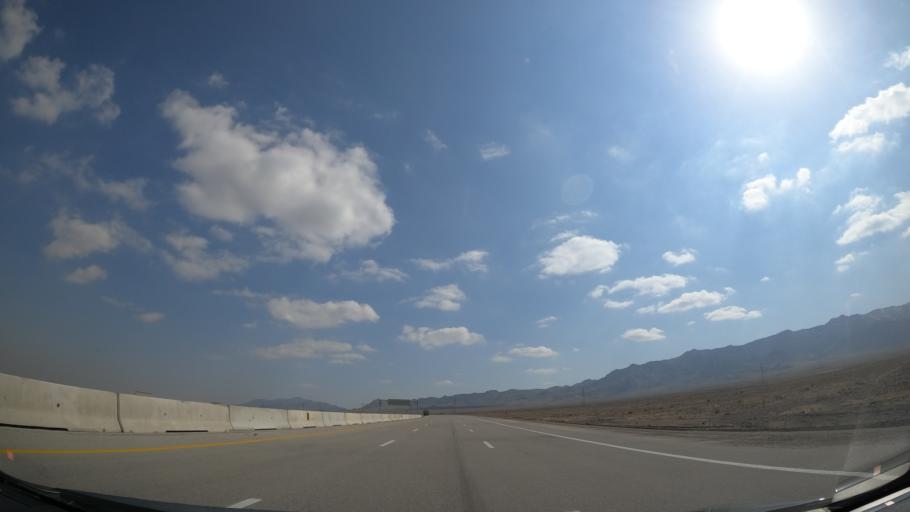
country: IR
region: Alborz
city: Eshtehard
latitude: 35.7202
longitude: 50.5707
